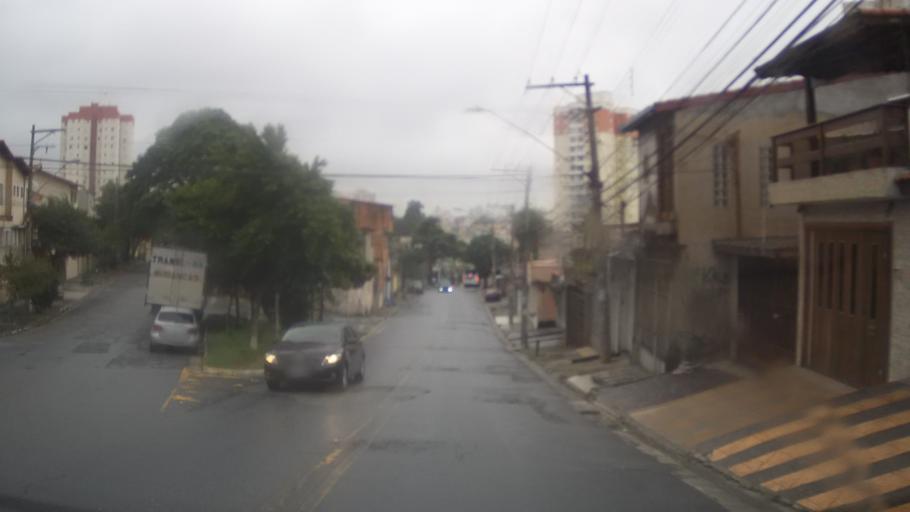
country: BR
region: Sao Paulo
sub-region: Guarulhos
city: Guarulhos
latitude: -23.4433
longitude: -46.5324
